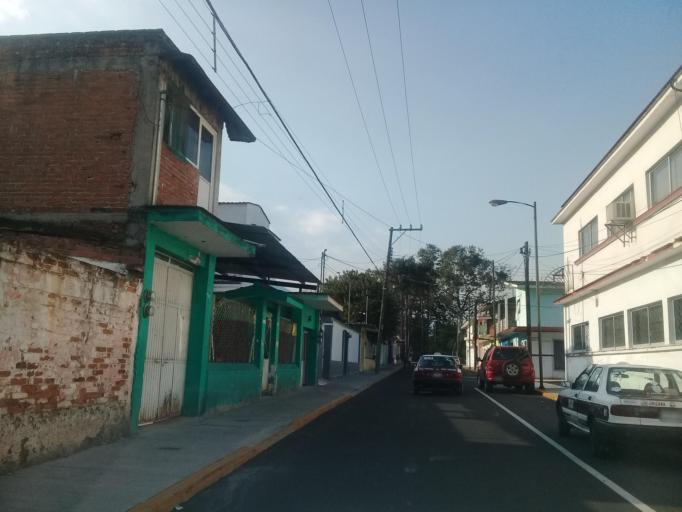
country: MX
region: Veracruz
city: Orizaba
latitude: 18.8530
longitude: -97.1127
